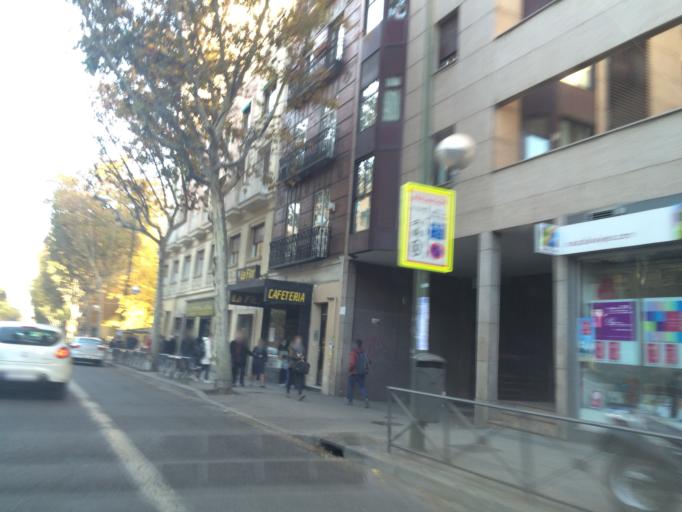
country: ES
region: Madrid
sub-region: Provincia de Madrid
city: Chamberi
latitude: 40.4297
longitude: -3.7063
